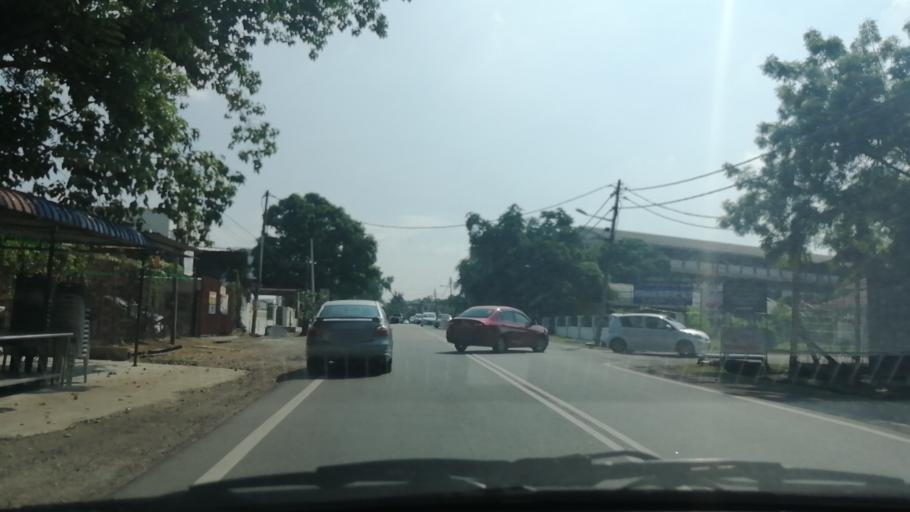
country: MY
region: Kedah
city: Sungai Petani
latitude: 5.6427
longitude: 100.4951
